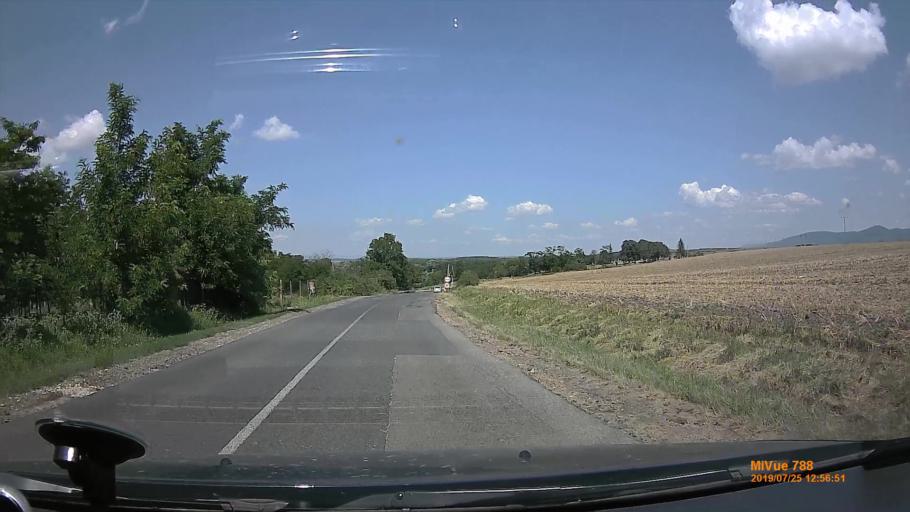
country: HU
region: Borsod-Abauj-Zemplen
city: Encs
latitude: 48.3148
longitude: 21.1659
